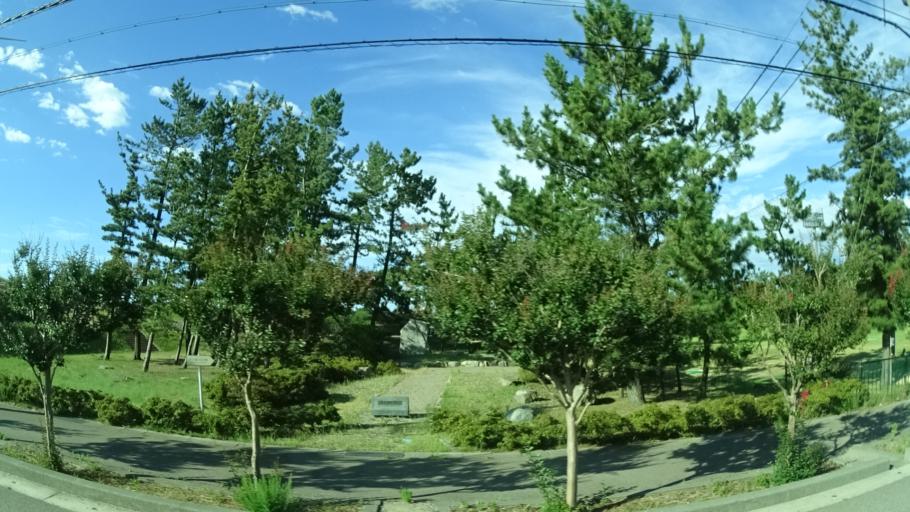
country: JP
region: Ishikawa
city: Kanazawa-shi
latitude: 36.6628
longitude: 136.6508
